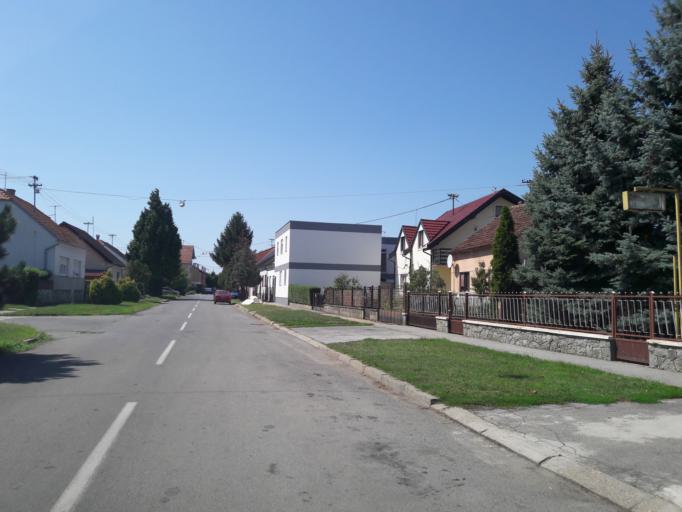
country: HR
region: Osjecko-Baranjska
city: Visnjevac
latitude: 45.5638
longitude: 18.6464
